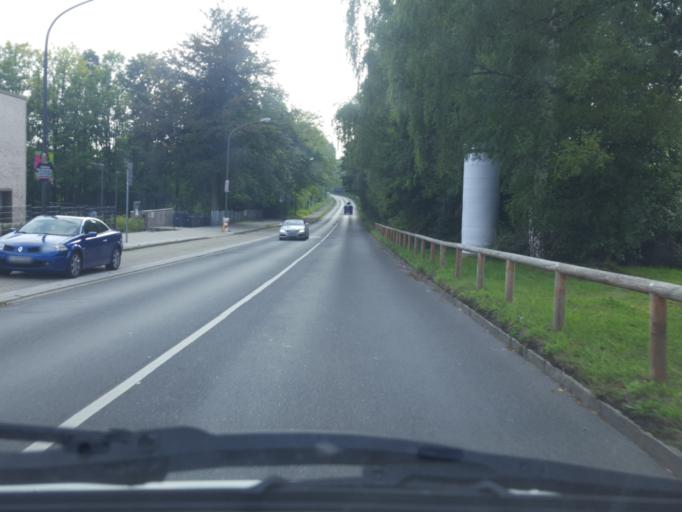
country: DE
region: North Rhine-Westphalia
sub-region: Regierungsbezirk Dusseldorf
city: Essen
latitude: 51.4162
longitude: 6.9557
